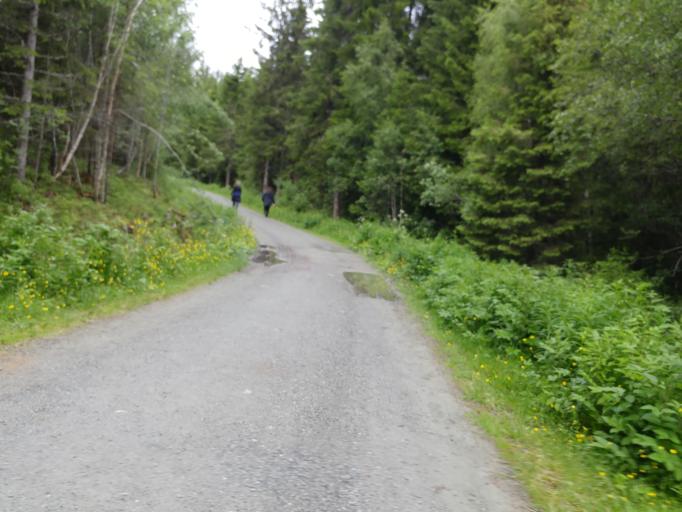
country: NO
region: Sor-Trondelag
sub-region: Melhus
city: Melhus
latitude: 63.3839
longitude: 10.2982
